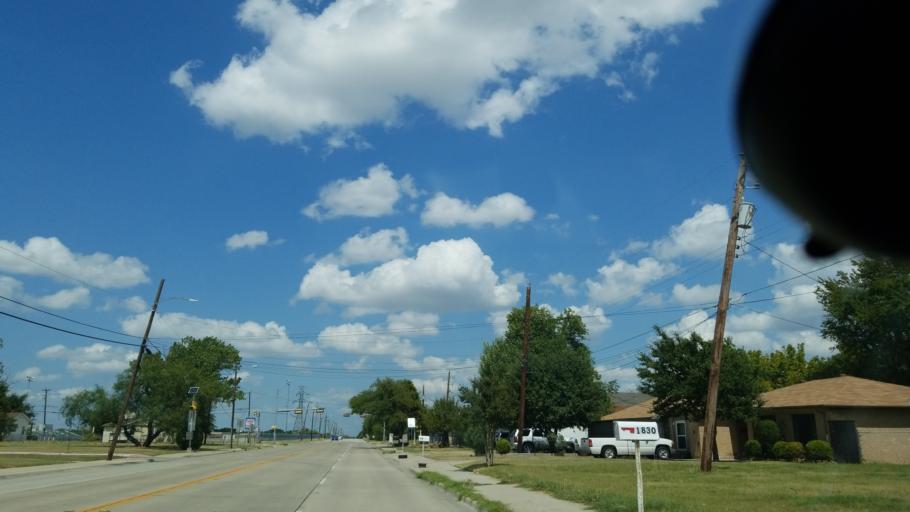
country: US
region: Texas
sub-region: Dallas County
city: Grand Prairie
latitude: 32.7193
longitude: -96.9858
